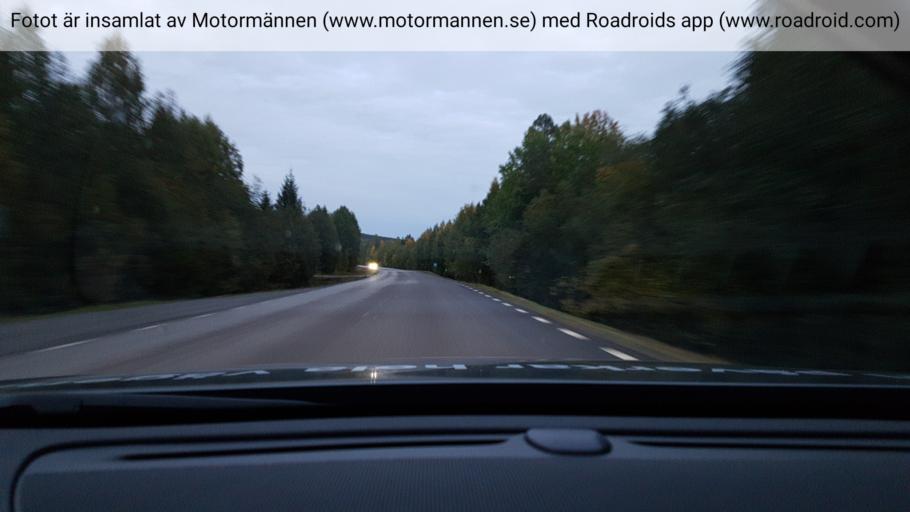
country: SE
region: Norrbotten
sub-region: Alvsbyns Kommun
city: AElvsbyn
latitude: 65.7818
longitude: 20.7765
